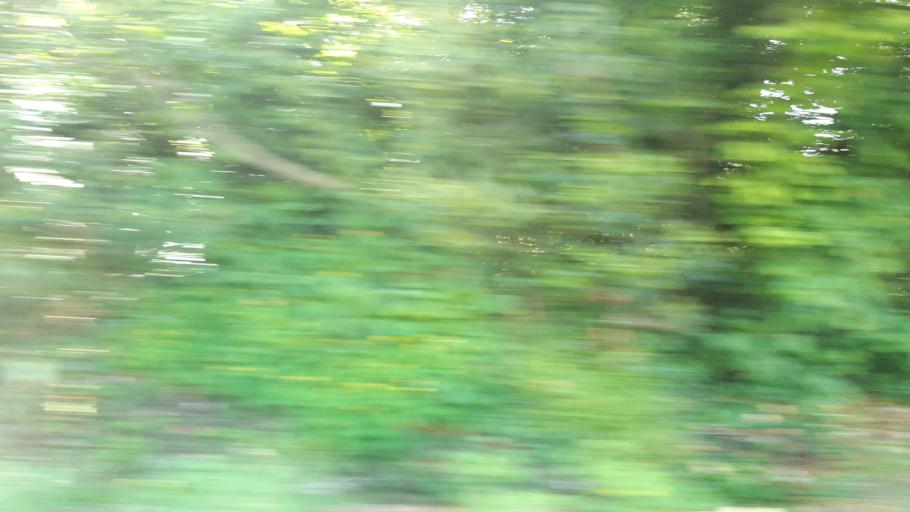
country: IT
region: Tuscany
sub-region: Provincia di Lucca
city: Capannori
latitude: 43.8684
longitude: 10.5706
